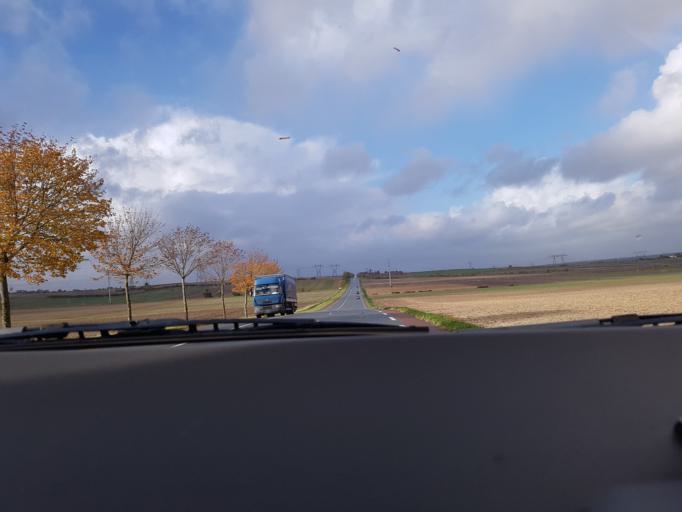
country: FR
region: Poitou-Charentes
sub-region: Departement de la Charente-Maritime
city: Les Gonds
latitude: 45.6643
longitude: -0.5956
